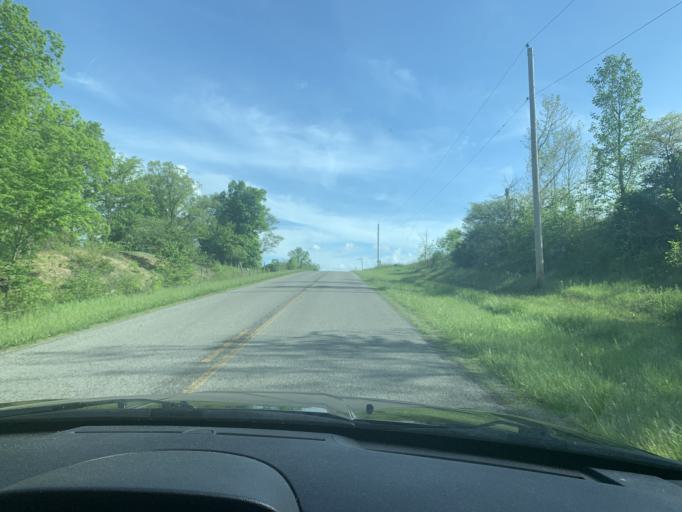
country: US
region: Ohio
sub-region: Logan County
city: De Graff
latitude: 40.3042
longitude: -84.0117
